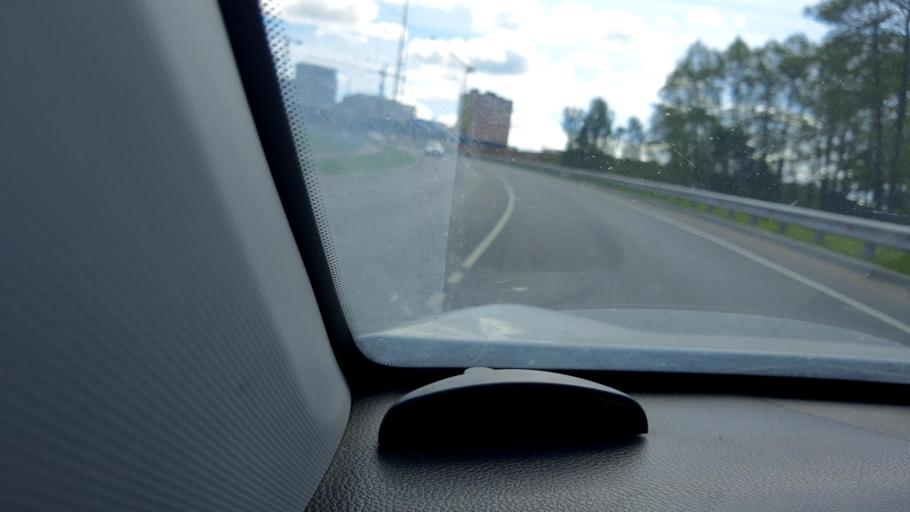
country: RU
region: Moskovskaya
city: Vidnoye
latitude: 55.5340
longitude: 37.7077
